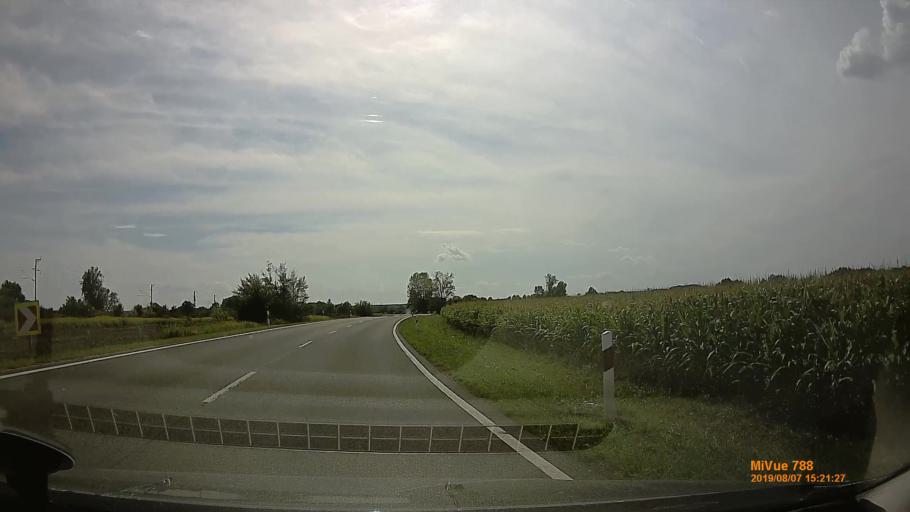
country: HU
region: Vas
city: Sarvar
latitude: 47.3375
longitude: 16.8648
